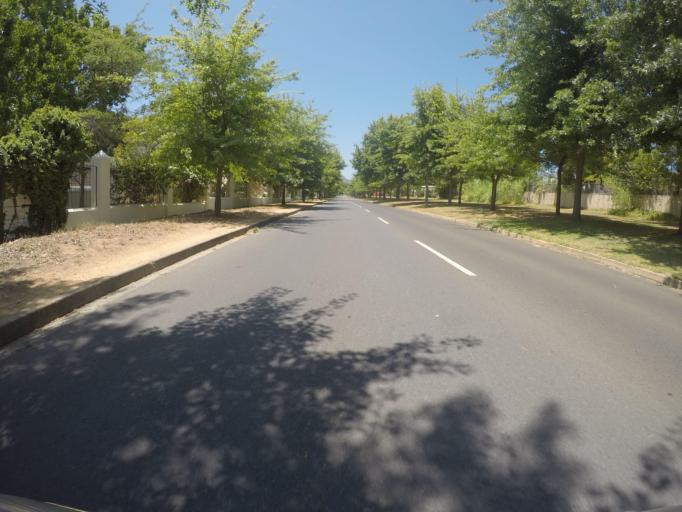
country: ZA
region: Western Cape
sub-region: Cape Winelands District Municipality
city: Stellenbosch
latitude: -33.9629
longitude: 18.8574
